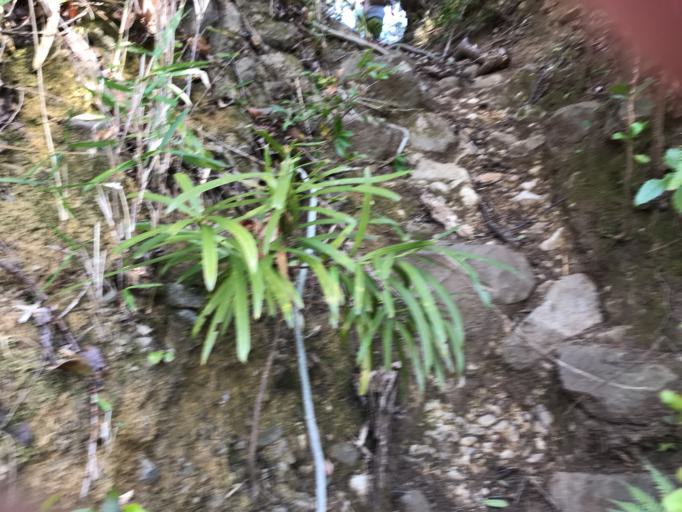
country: JP
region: Shizuoka
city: Numazu
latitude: 35.0539
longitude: 138.8969
